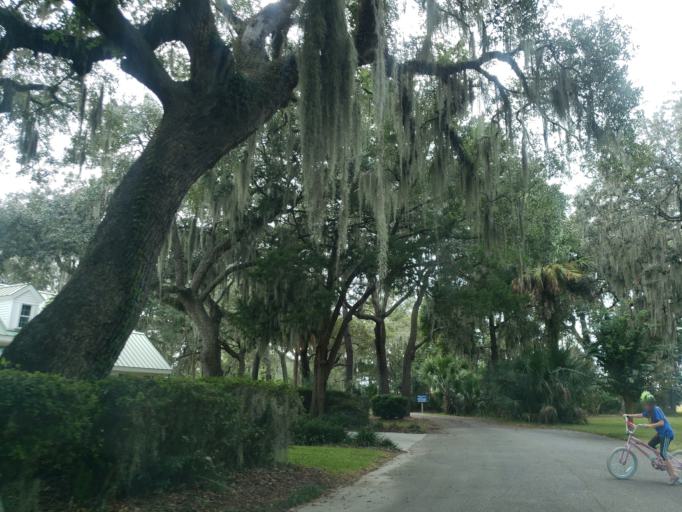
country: US
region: Georgia
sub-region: Chatham County
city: Montgomery
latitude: 31.9502
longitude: -81.1244
